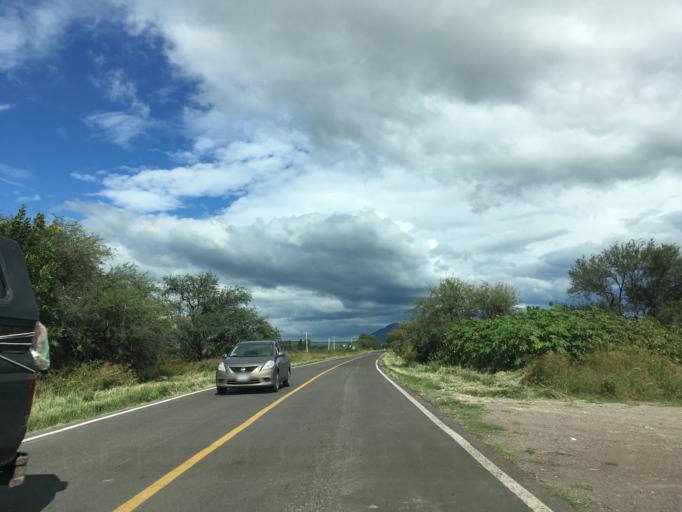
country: MX
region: Michoacan
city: Santa Ana Maya
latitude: 20.0449
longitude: -101.0705
